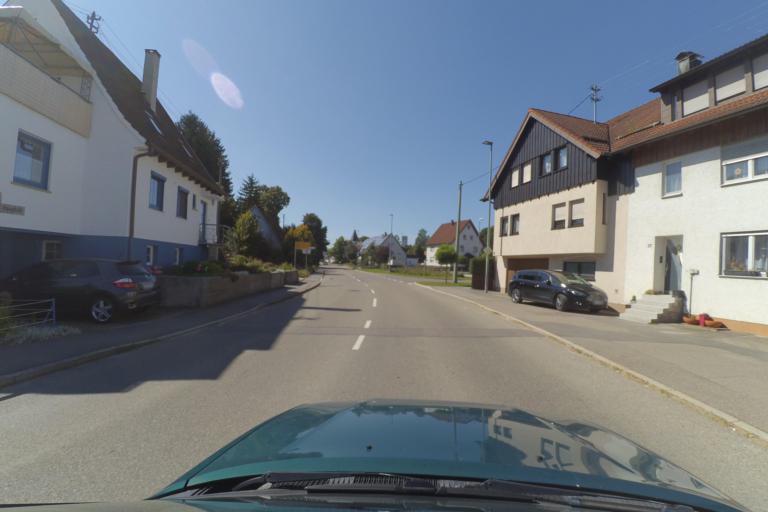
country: DE
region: Baden-Wuerttemberg
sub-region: Regierungsbezirk Stuttgart
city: Bartholoma
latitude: 48.7535
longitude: 9.9932
